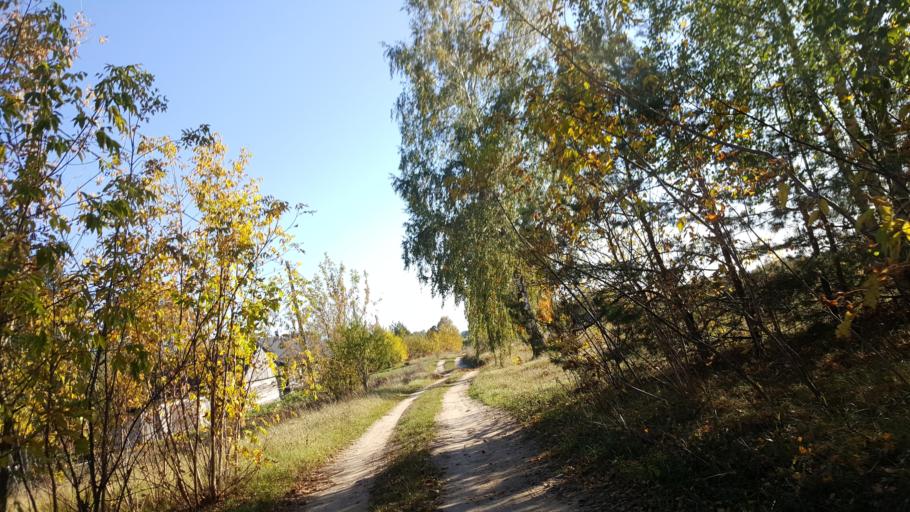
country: BY
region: Brest
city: Kamyanyets
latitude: 52.3893
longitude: 23.8841
